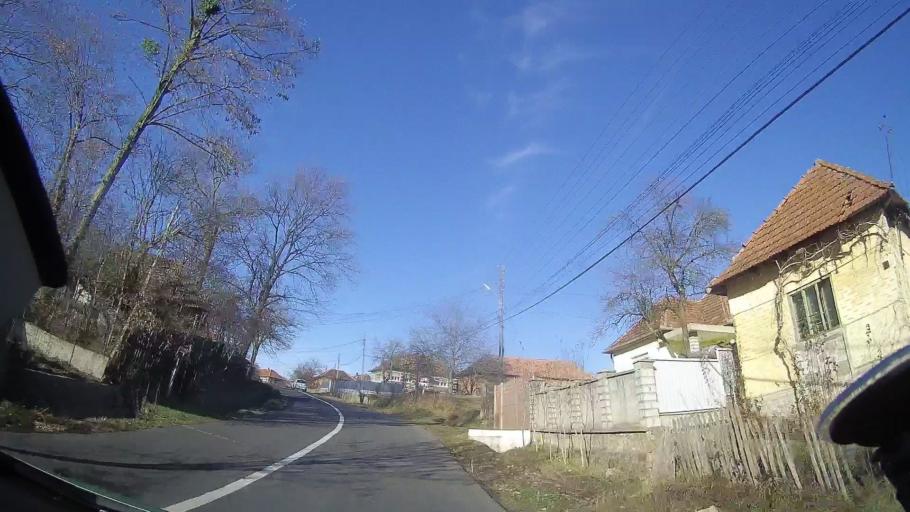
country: RO
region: Bihor
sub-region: Comuna Bratca
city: Beznea
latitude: 46.9599
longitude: 22.6175
